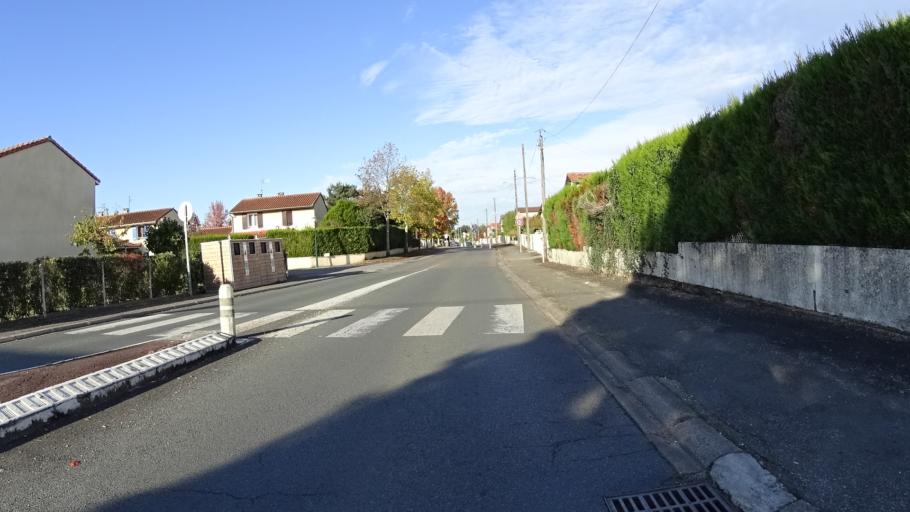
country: FR
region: Aquitaine
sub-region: Departement des Landes
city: Saint-Paul-les-Dax
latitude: 43.7318
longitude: -1.0563
